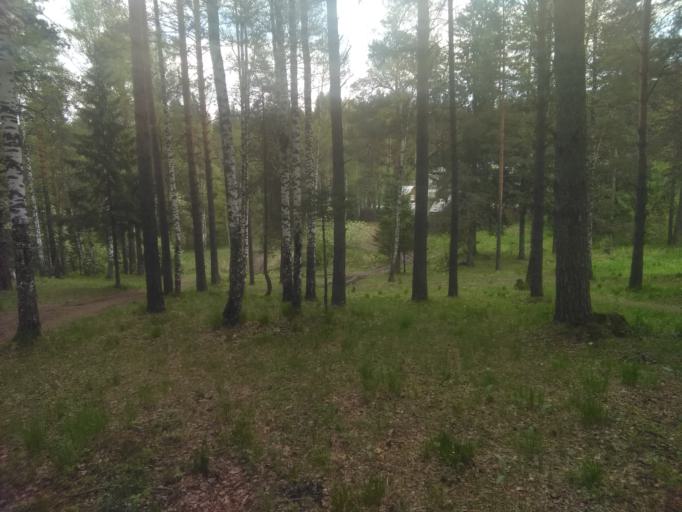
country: RU
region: Chelyabinsk
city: Zlatoust
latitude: 55.1249
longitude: 59.7363
